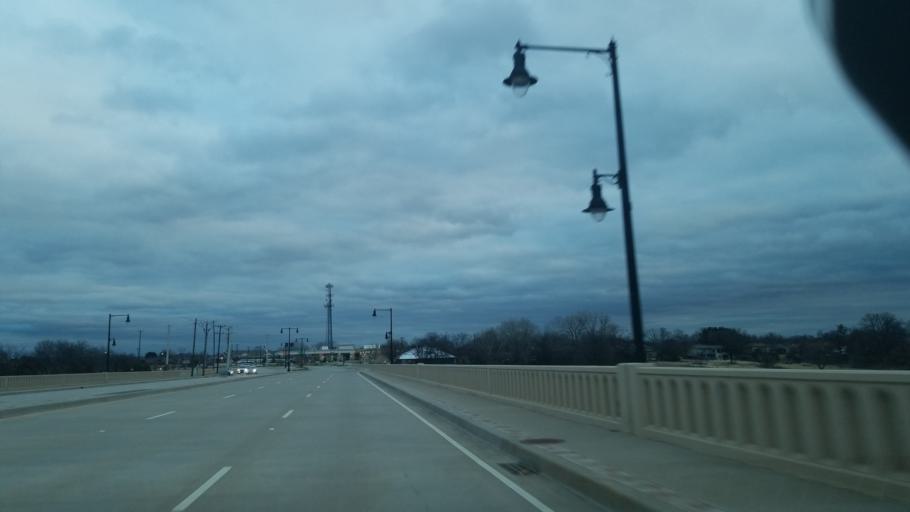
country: US
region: Texas
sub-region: Denton County
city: Little Elm
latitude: 33.1568
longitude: -96.9519
